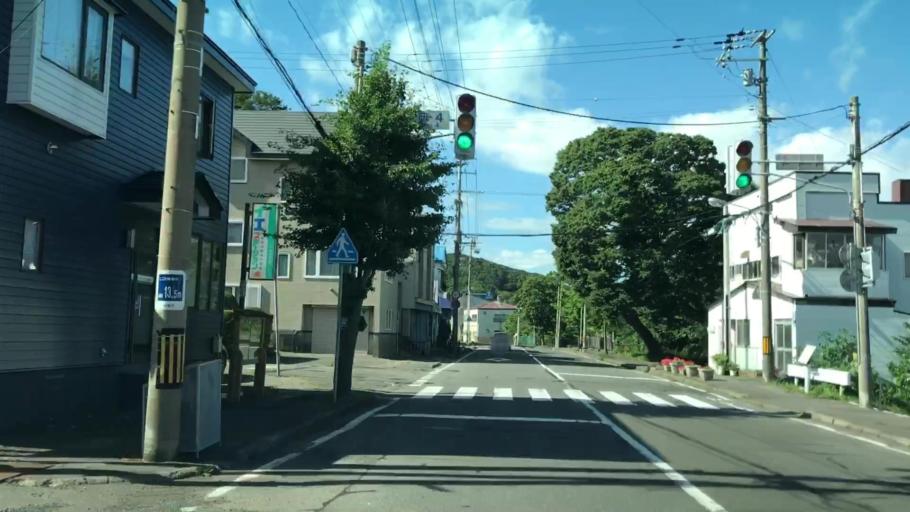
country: JP
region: Hokkaido
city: Muroran
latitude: 42.3222
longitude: 140.9690
